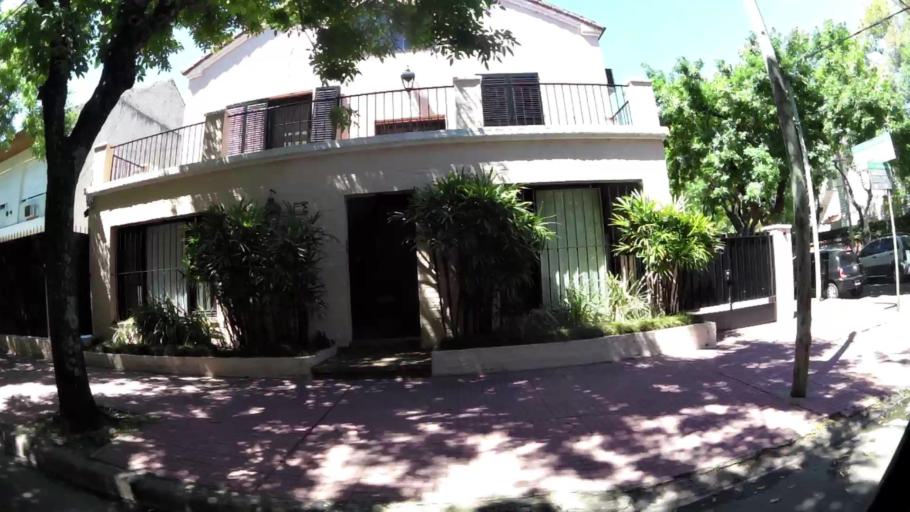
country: AR
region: Buenos Aires
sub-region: Partido de San Isidro
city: San Isidro
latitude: -34.4810
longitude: -58.4907
